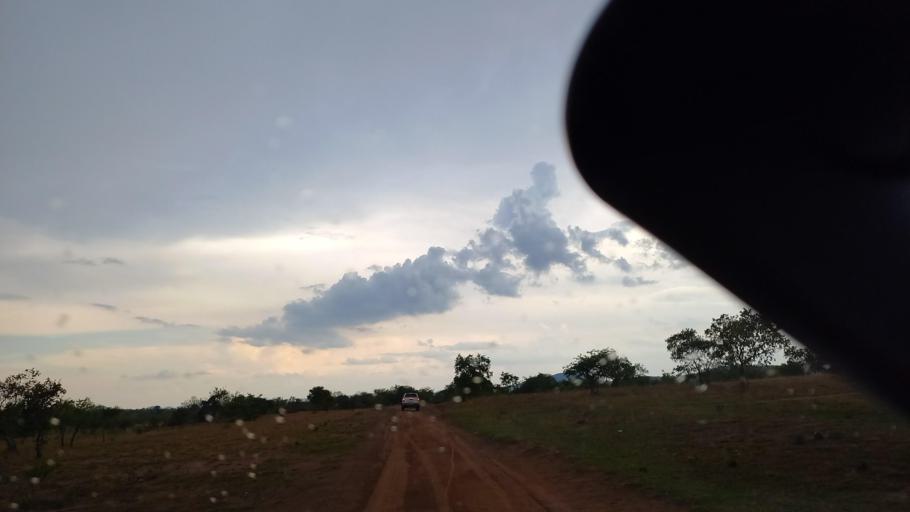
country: ZM
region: Lusaka
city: Kafue
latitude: -15.9762
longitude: 28.2539
